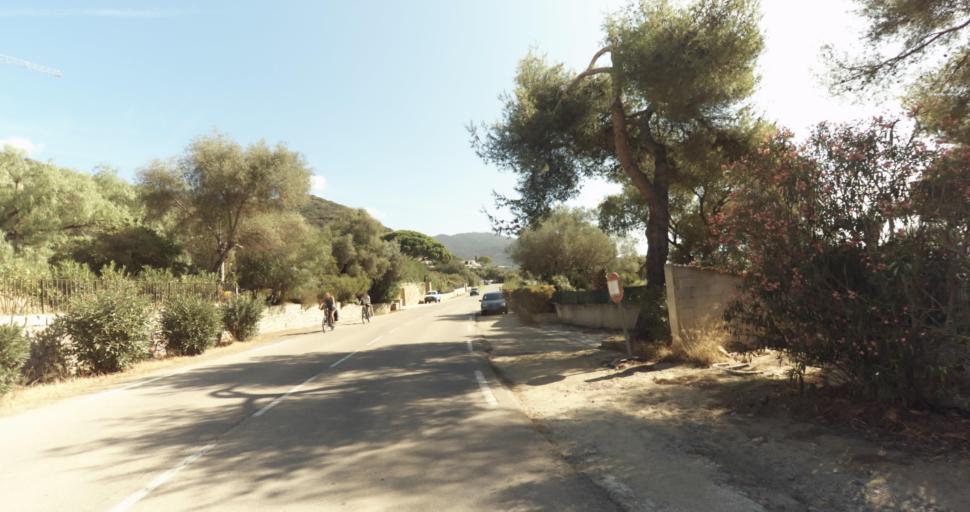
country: FR
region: Corsica
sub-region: Departement de la Corse-du-Sud
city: Ajaccio
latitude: 41.9068
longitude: 8.6289
